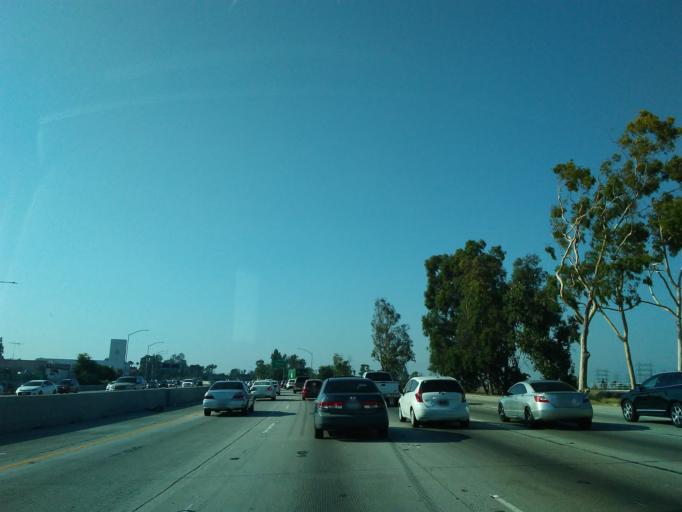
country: US
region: California
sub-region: Los Angeles County
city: East Rancho Dominguez
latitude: 33.9249
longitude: -118.1777
